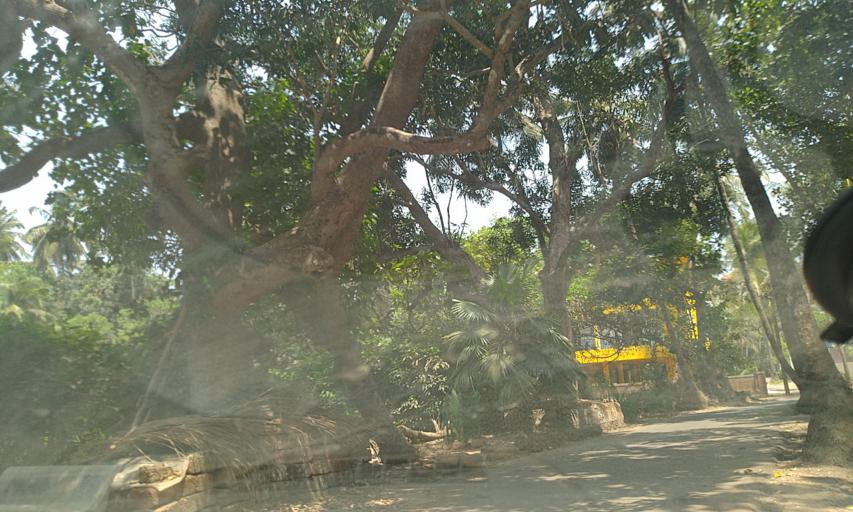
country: IN
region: Goa
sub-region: North Goa
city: Saligao
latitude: 15.5507
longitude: 73.7862
